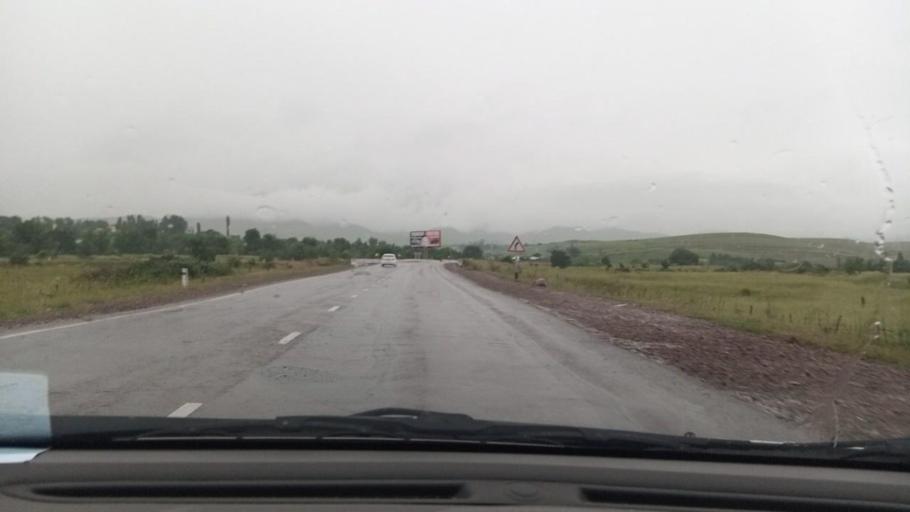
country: UZ
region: Toshkent
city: Angren
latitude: 41.0481
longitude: 70.1586
